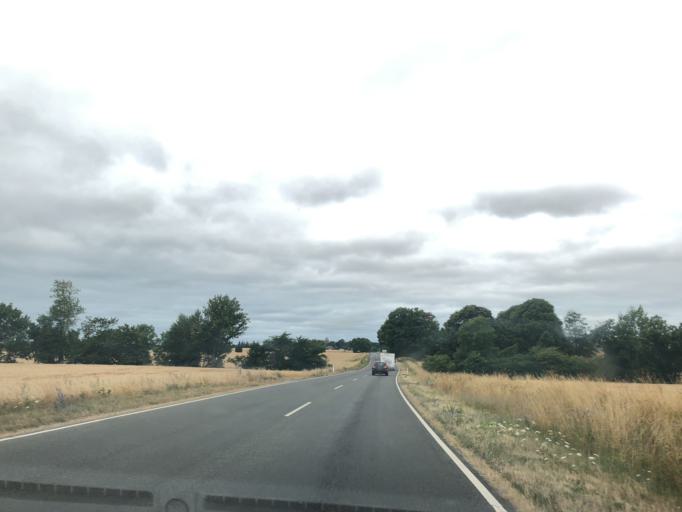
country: DK
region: Zealand
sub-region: Slagelse Kommune
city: Skaelskor
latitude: 55.3014
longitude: 11.2984
